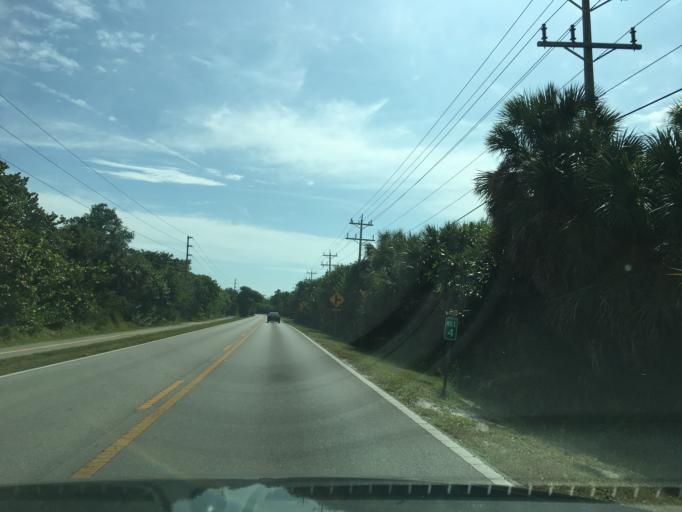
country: US
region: Florida
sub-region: Lee County
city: Saint James City
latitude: 26.4575
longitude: -82.1438
